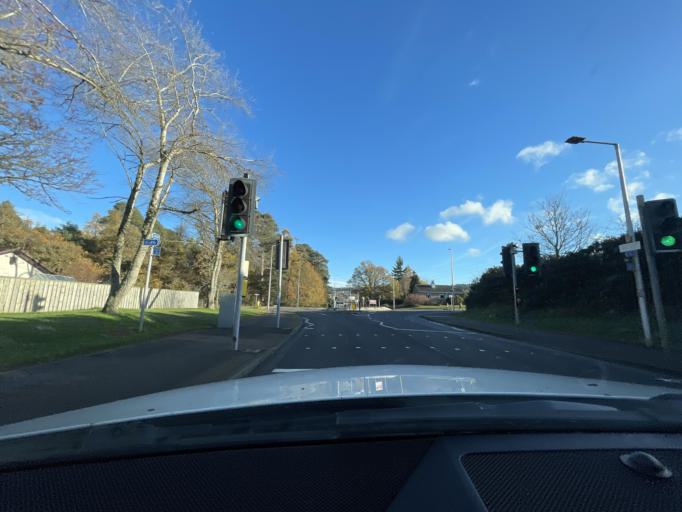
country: GB
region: Scotland
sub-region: Highland
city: Inverness
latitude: 57.4480
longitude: -4.2396
